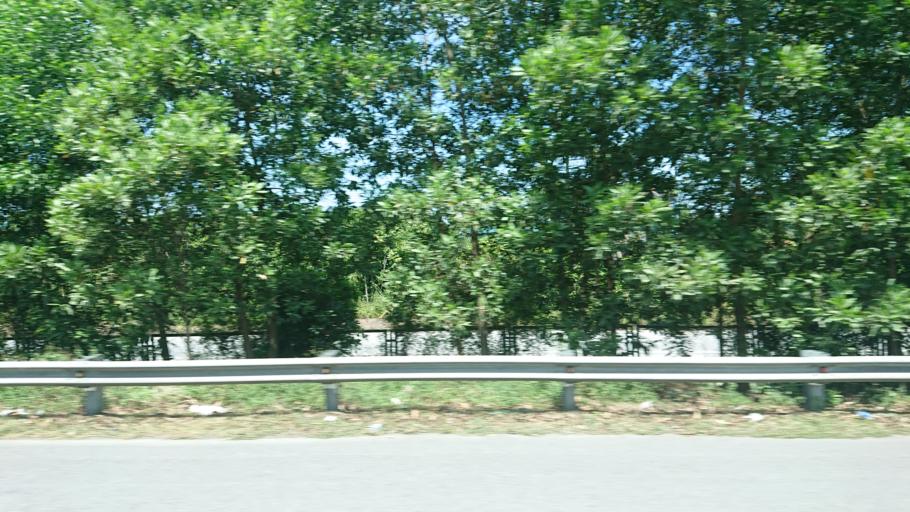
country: VN
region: Ha Nam
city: Thi Tran Hoa Mac
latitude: 20.6038
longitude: 105.9484
